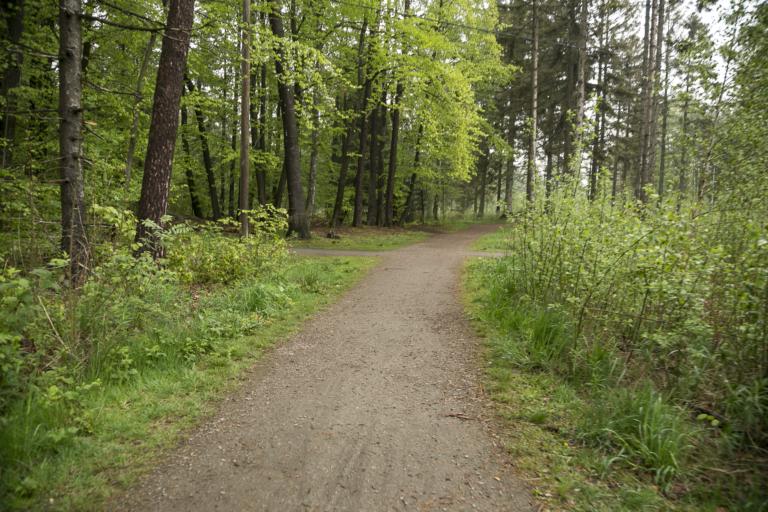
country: SE
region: Halland
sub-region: Varbergs Kommun
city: Varberg
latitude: 57.0974
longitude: 12.2701
